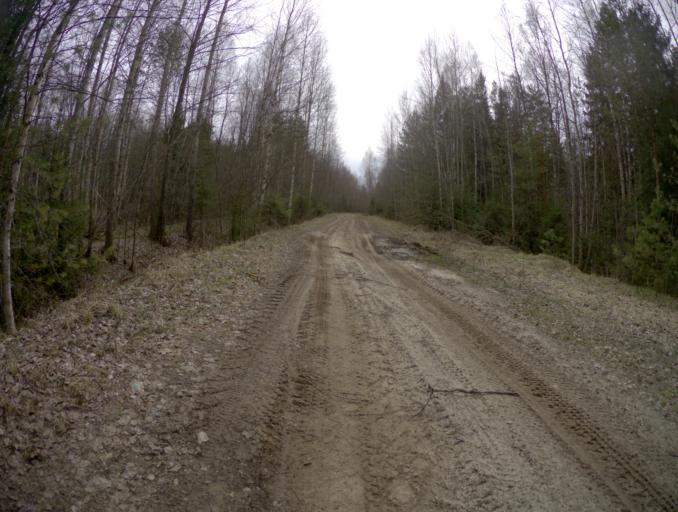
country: RU
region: Vladimir
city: Raduzhnyy
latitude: 55.9340
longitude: 40.2439
